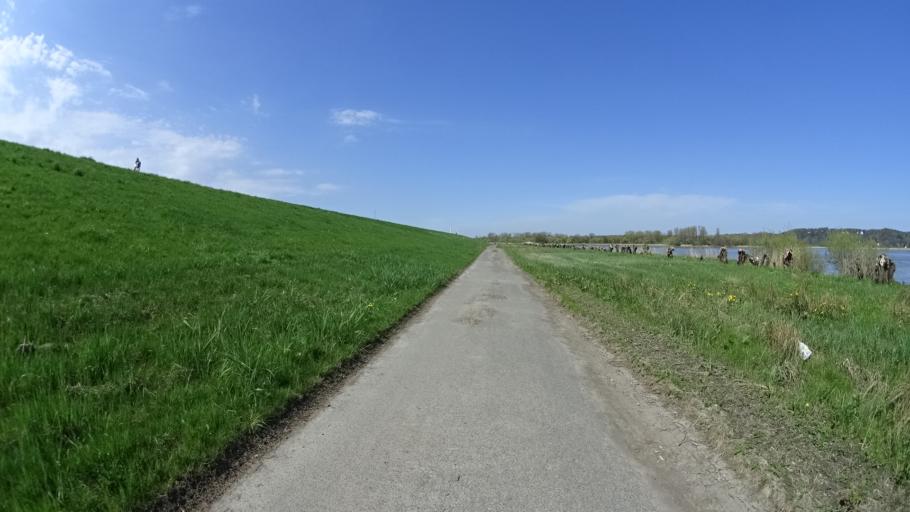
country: DE
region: Schleswig-Holstein
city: Wedel
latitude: 53.5443
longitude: 9.7693
